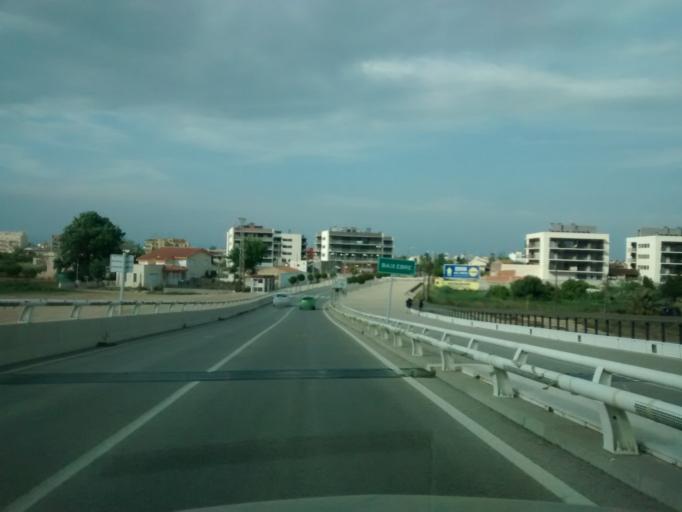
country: ES
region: Catalonia
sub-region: Provincia de Tarragona
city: Deltebre
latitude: 40.7140
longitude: 0.7178
